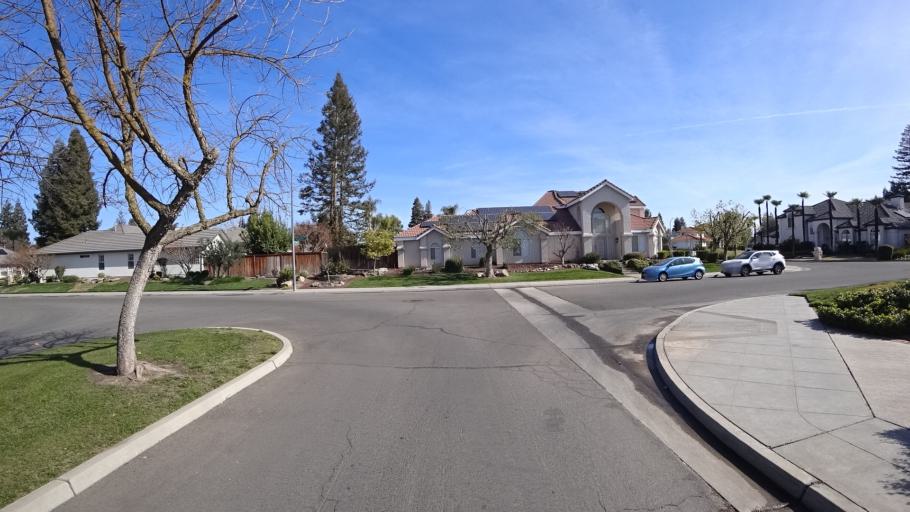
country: US
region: California
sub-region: Fresno County
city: Clovis
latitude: 36.8911
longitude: -119.7693
